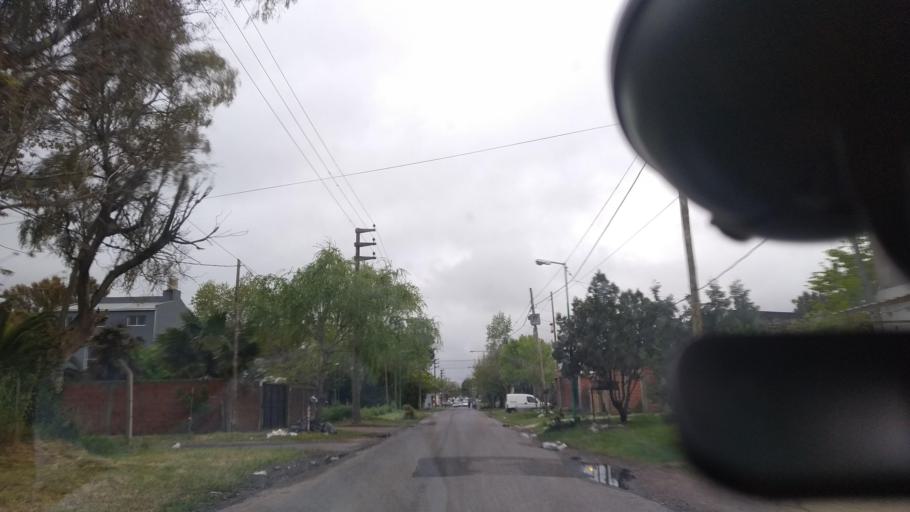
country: AR
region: Buenos Aires
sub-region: Partido de La Plata
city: La Plata
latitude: -34.9498
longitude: -57.9899
